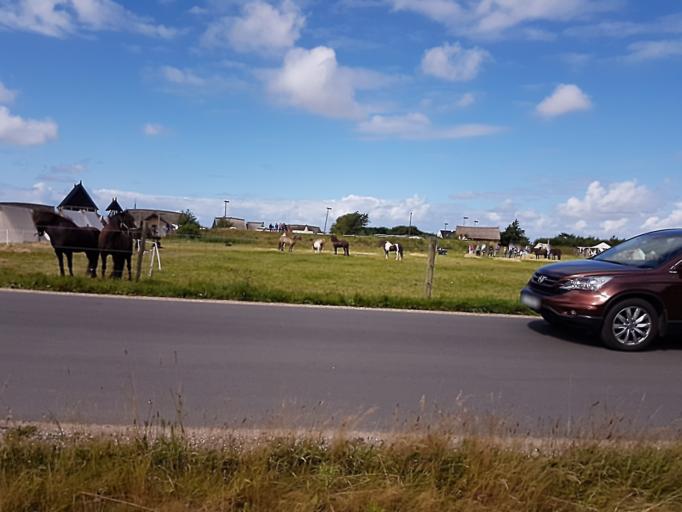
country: DK
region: South Denmark
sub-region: Varde Kommune
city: Oksbol
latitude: 55.8368
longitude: 8.2690
